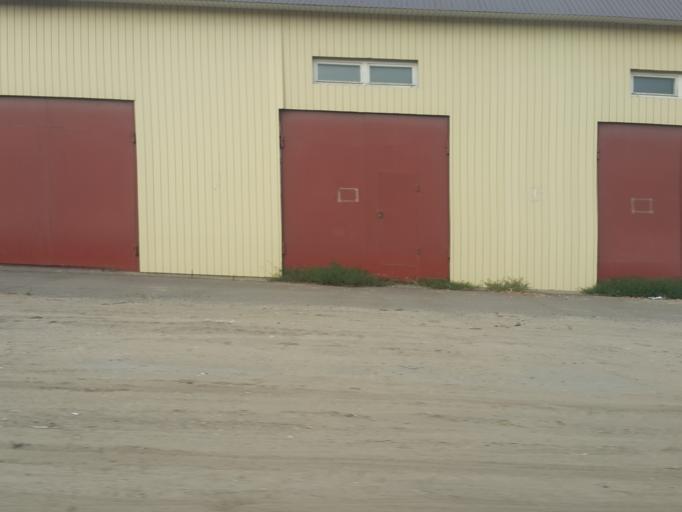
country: RU
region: Tambov
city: Bokino
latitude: 52.6412
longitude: 41.4404
